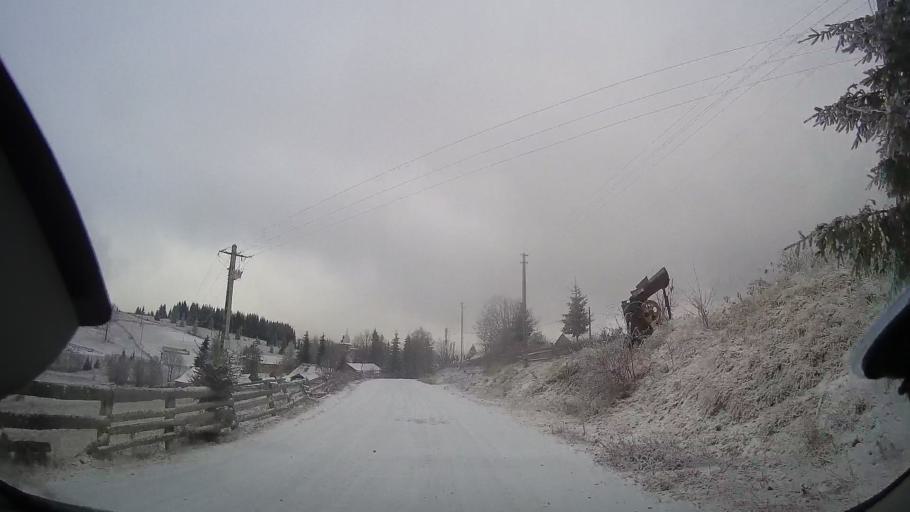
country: RO
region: Cluj
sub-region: Comuna Marisel
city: Marisel
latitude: 46.6596
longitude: 23.1303
